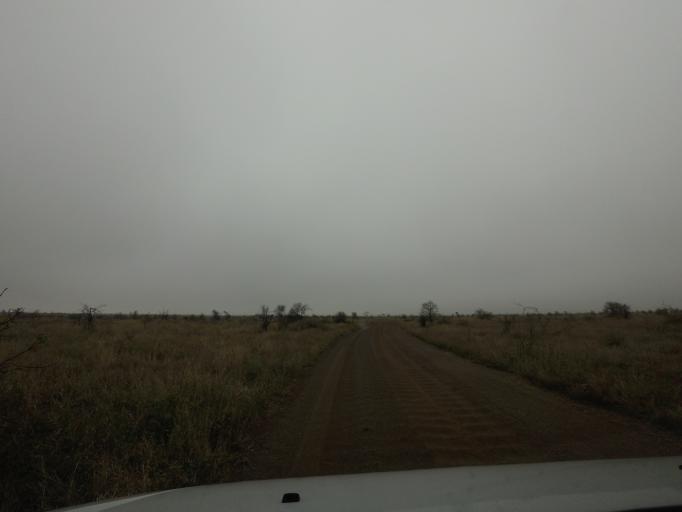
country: ZA
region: Limpopo
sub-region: Mopani District Municipality
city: Phalaborwa
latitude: -24.2569
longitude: 31.6869
